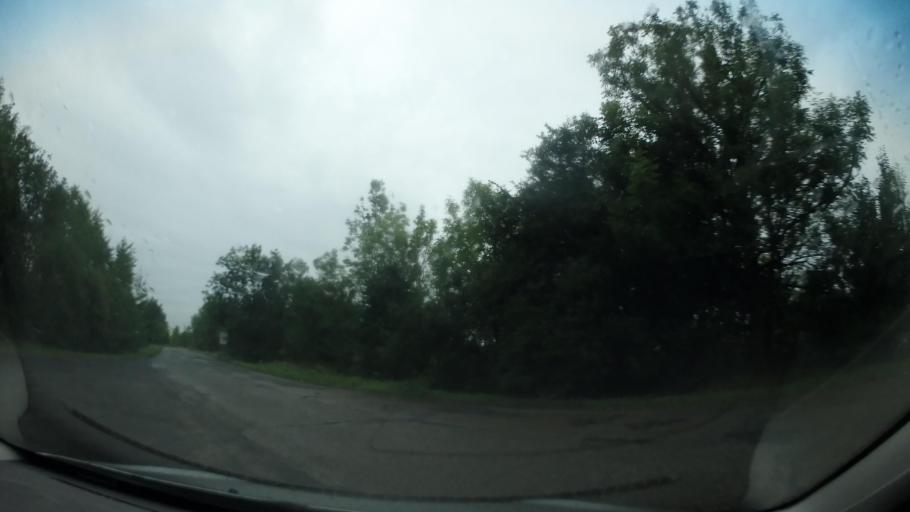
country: CZ
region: Central Bohemia
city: Milovice
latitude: 50.2417
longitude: 14.8970
